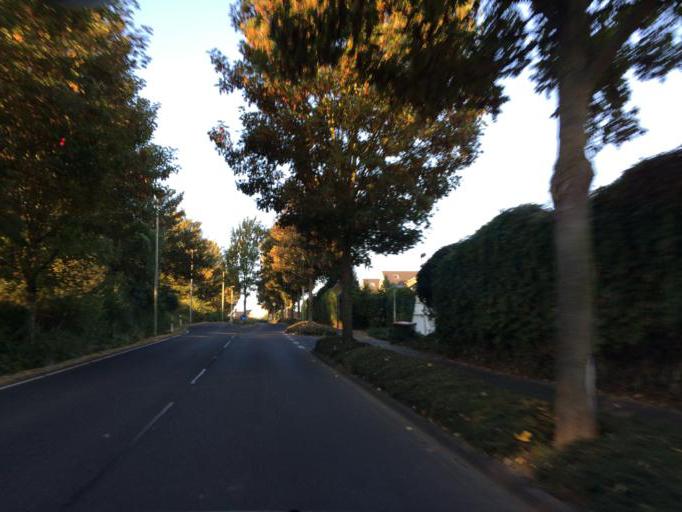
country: DE
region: North Rhine-Westphalia
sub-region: Regierungsbezirk Koln
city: Konigswinter
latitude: 50.6622
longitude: 7.1757
